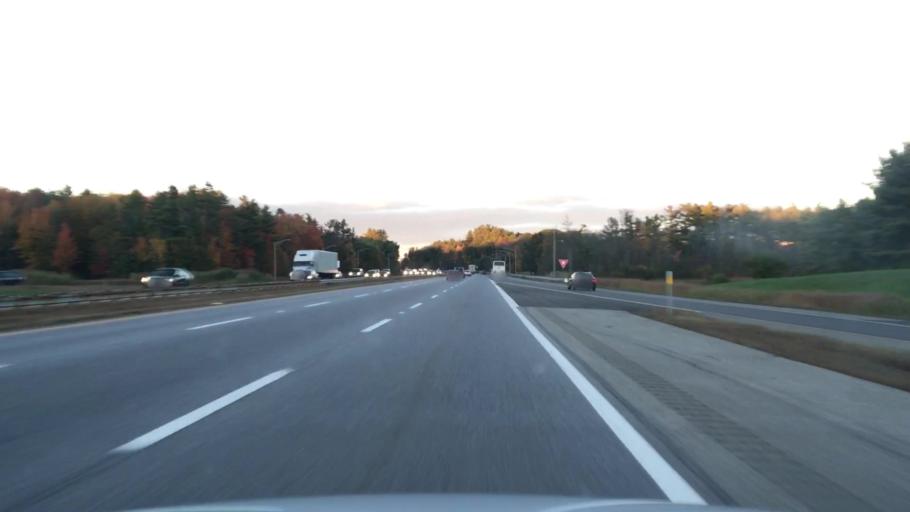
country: US
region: Maine
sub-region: York County
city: Biddeford
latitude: 43.4817
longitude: -70.4982
